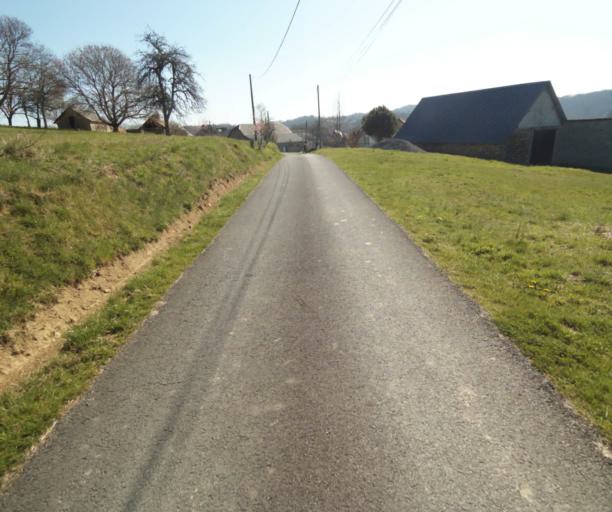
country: FR
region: Limousin
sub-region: Departement de la Correze
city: Saint-Mexant
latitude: 45.2991
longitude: 1.6154
